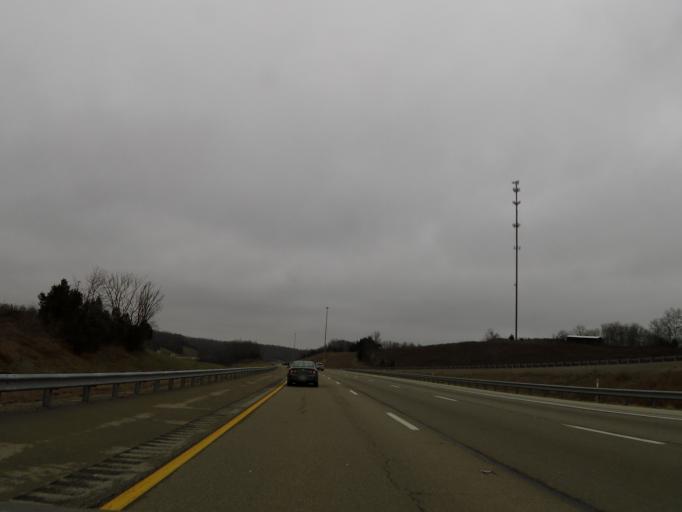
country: US
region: Kentucky
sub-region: Grant County
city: Williamstown
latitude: 38.4889
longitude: -84.5863
